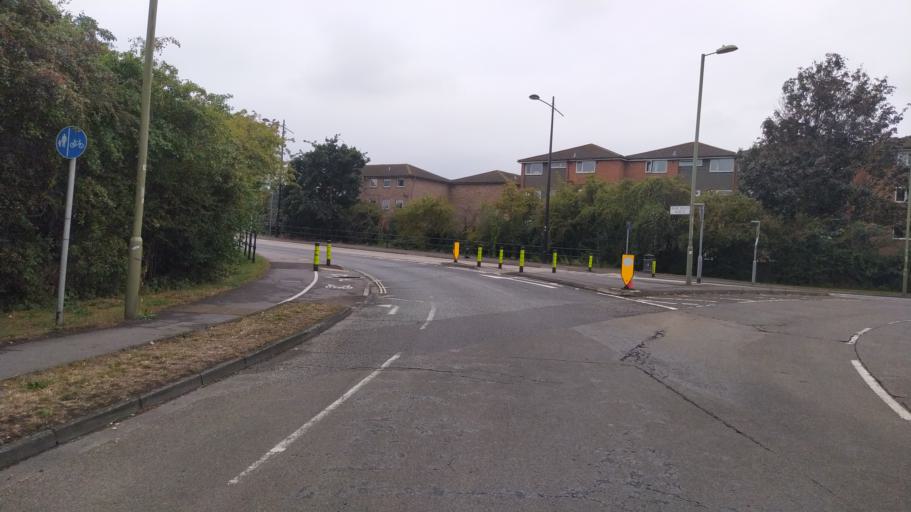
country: GB
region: England
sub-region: Hampshire
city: Havant
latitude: 50.8563
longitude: -0.9857
